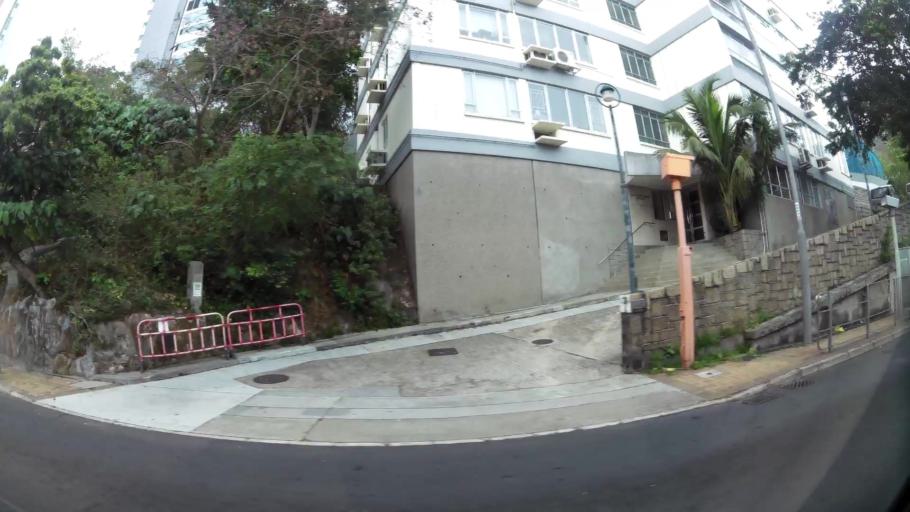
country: HK
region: Central and Western
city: Central
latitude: 22.2671
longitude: 114.1323
